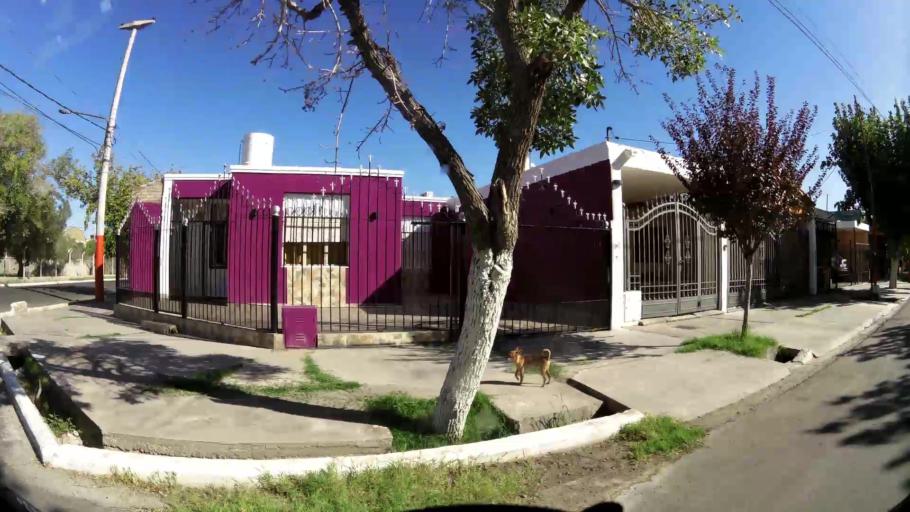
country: AR
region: San Juan
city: Villa Paula de Sarmiento
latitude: -31.5076
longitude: -68.5223
